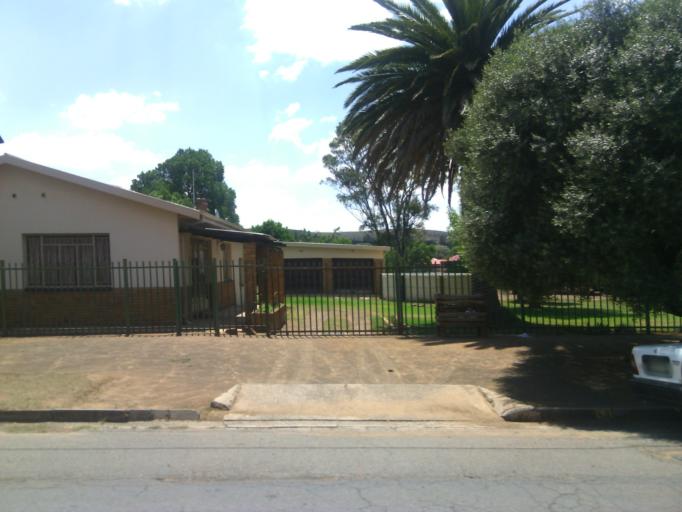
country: ZA
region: Orange Free State
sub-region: Xhariep District Municipality
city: Dewetsdorp
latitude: -29.5811
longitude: 26.6688
